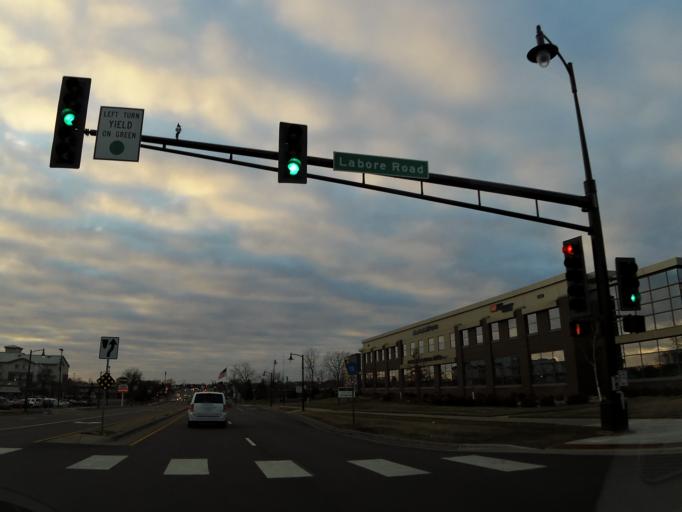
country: US
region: Minnesota
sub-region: Ramsey County
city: Vadnais Heights
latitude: 45.0504
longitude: -93.0513
